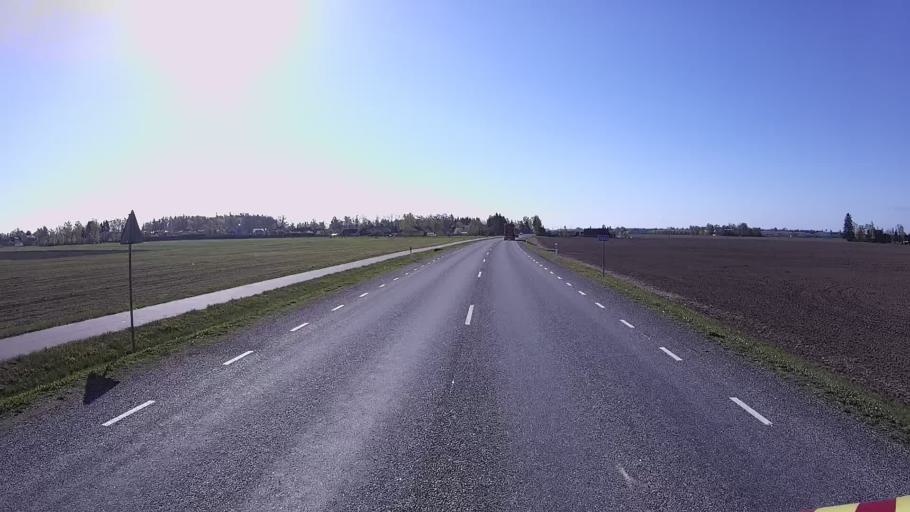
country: EE
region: Jaervamaa
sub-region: Paide linn
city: Paide
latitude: 58.7602
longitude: 25.5531
